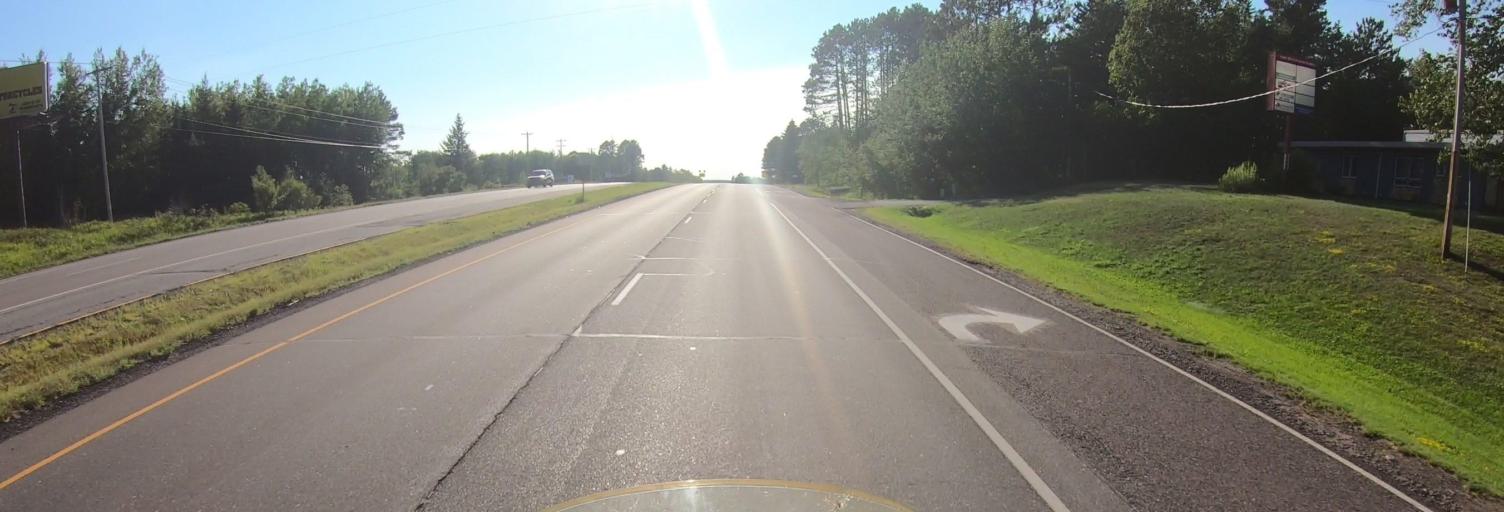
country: US
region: Minnesota
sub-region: Saint Louis County
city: Hermantown
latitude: 46.8367
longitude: -92.2324
